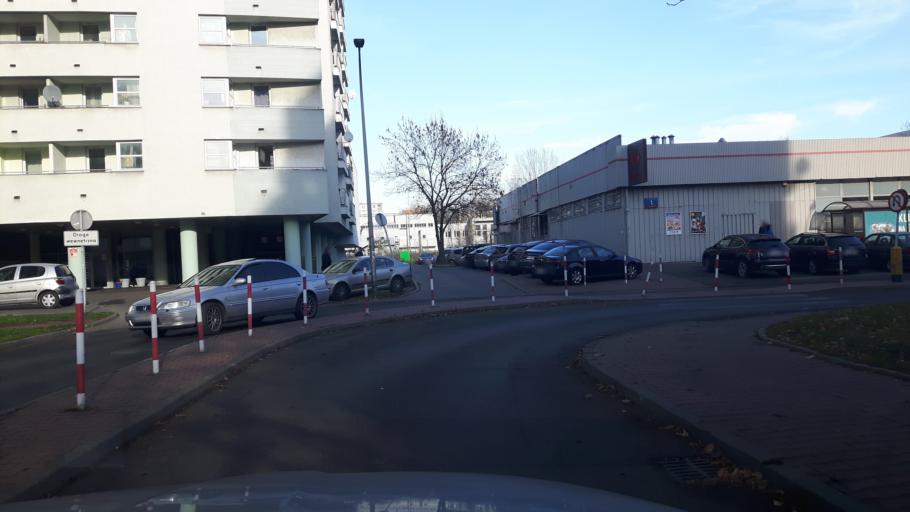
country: PL
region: Masovian Voivodeship
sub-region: Warszawa
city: Ochota
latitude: 52.2001
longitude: 20.9689
